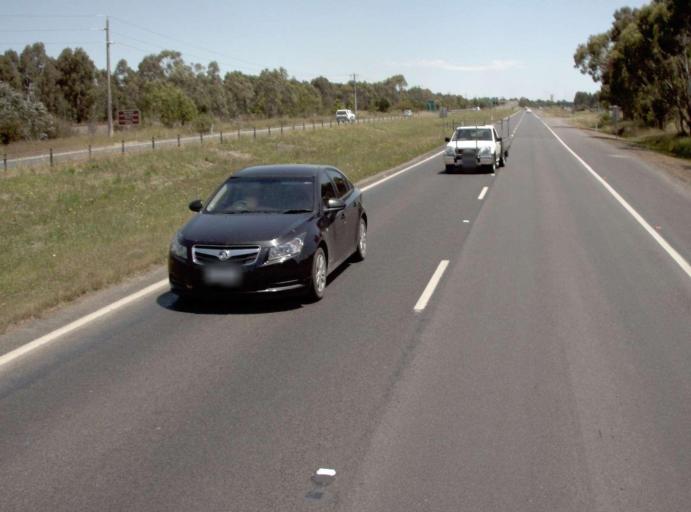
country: AU
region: Victoria
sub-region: Latrobe
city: Morwell
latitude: -38.2220
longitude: 146.4696
